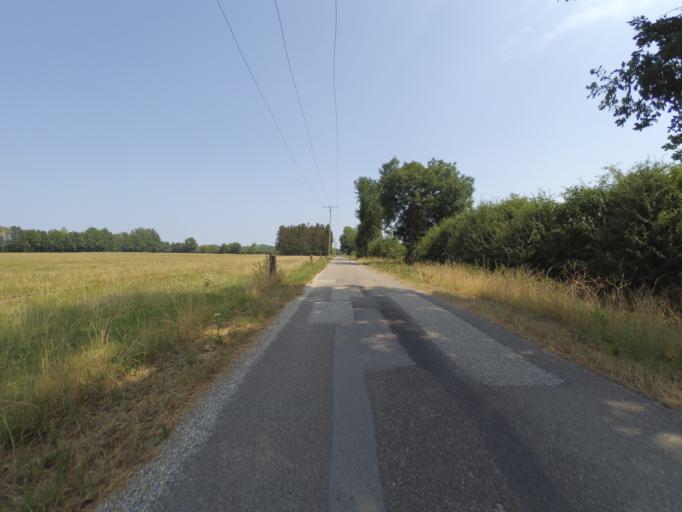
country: DE
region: North Rhine-Westphalia
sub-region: Regierungsbezirk Dusseldorf
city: Mehrhoog
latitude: 51.7462
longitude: 6.4706
